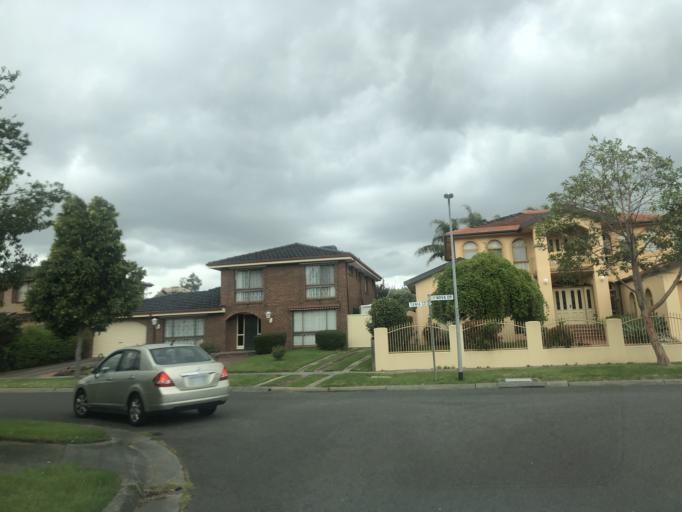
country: AU
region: Victoria
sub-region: Casey
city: Doveton
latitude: -37.9866
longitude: 145.2269
